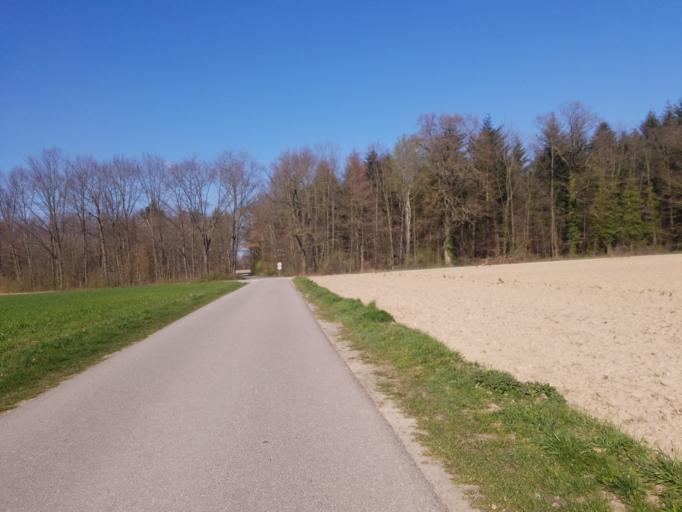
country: DE
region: Baden-Wuerttemberg
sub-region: Karlsruhe Region
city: Schwarzach
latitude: 48.7543
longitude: 8.0681
